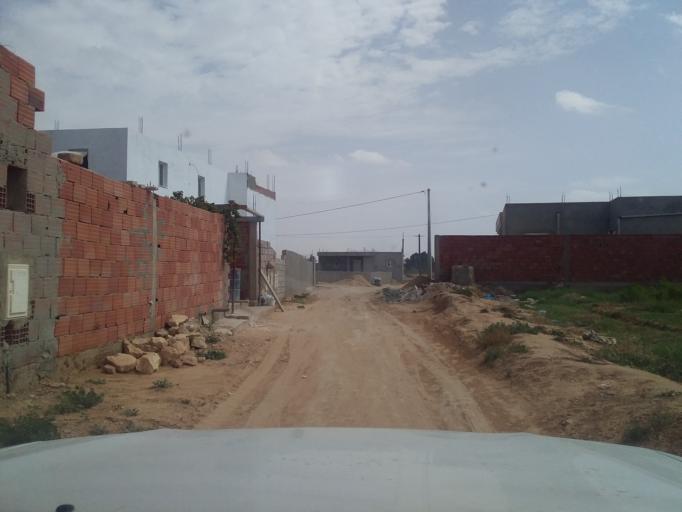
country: TN
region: Qabis
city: Matmata
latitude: 33.6133
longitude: 10.2761
